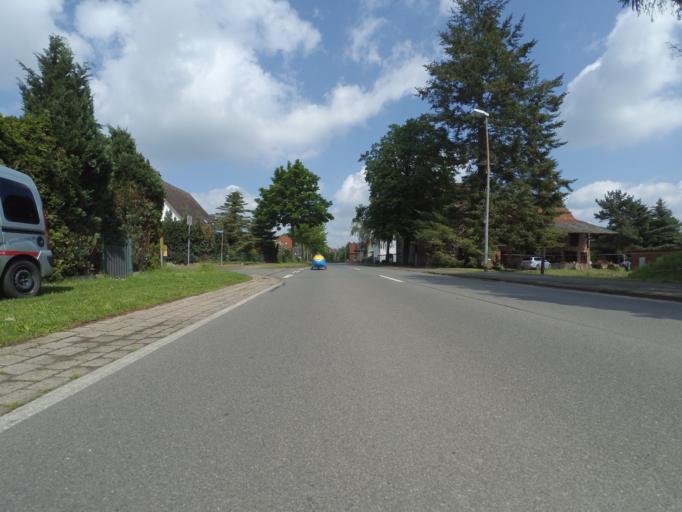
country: DE
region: Lower Saxony
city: Didderse
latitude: 52.3964
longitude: 10.3451
